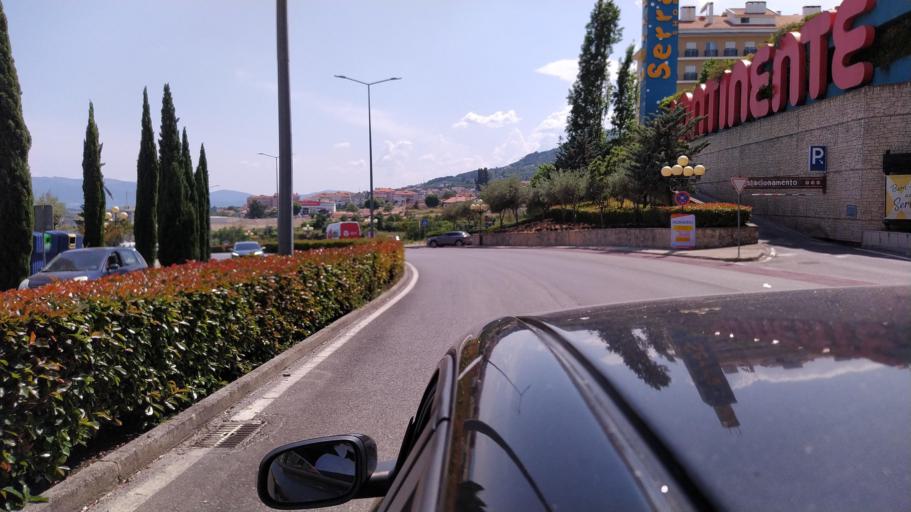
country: PT
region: Castelo Branco
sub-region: Covilha
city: Covilha
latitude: 40.2705
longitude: -7.5018
